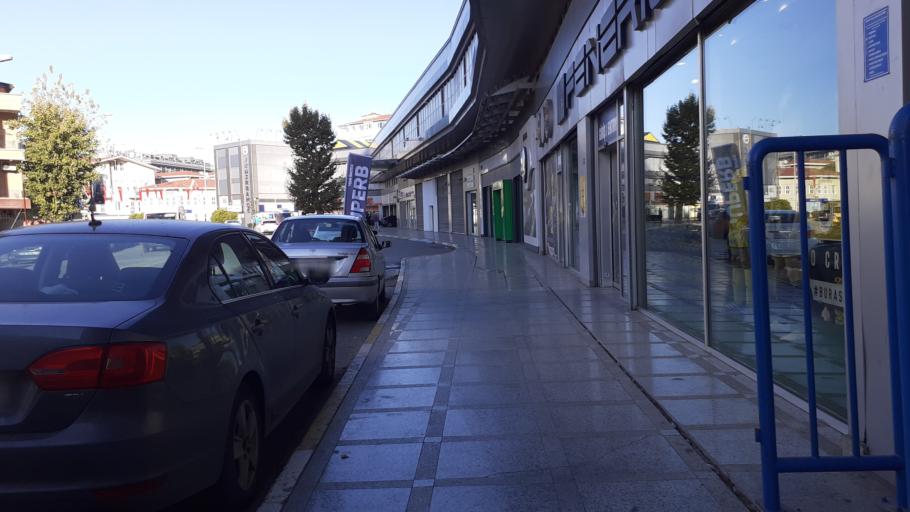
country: TR
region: Istanbul
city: UEskuedar
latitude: 40.9868
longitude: 29.0364
